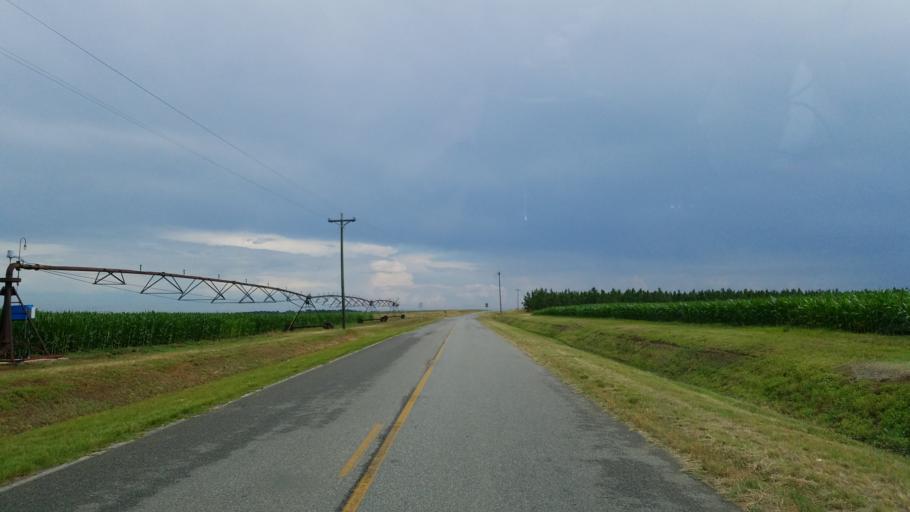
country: US
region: Georgia
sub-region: Dooly County
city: Unadilla
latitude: 32.2921
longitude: -83.7914
